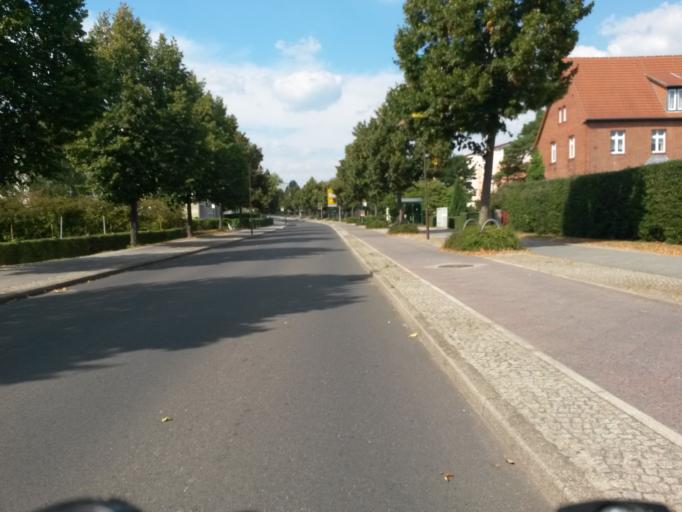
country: DE
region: Brandenburg
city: Templin
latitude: 53.1114
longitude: 13.5159
